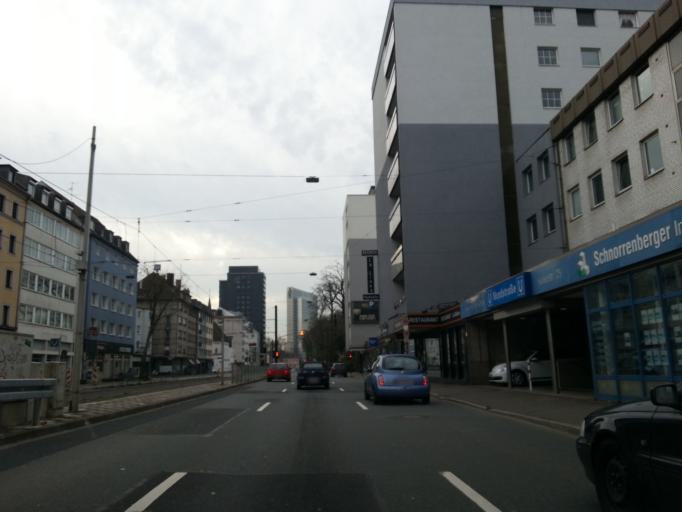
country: DE
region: North Rhine-Westphalia
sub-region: Regierungsbezirk Dusseldorf
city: Dusseldorf
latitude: 51.2339
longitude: 6.7786
